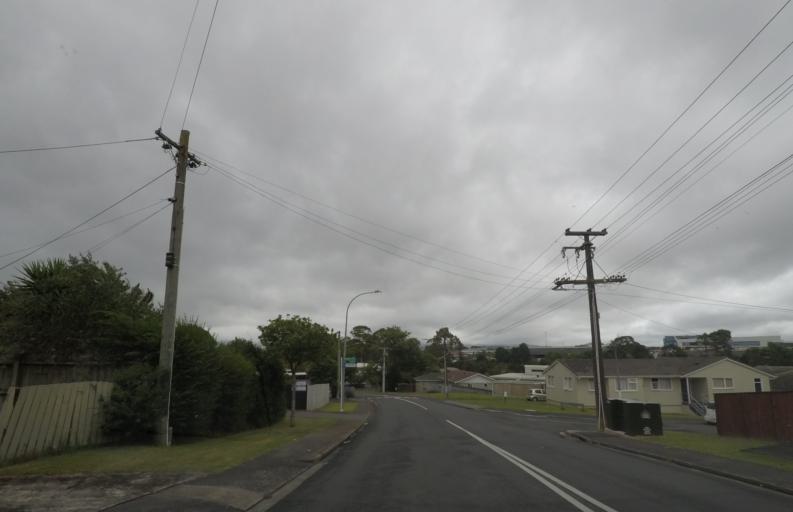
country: NZ
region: Auckland
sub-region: Auckland
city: Rosebank
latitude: -36.8639
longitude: 174.6398
